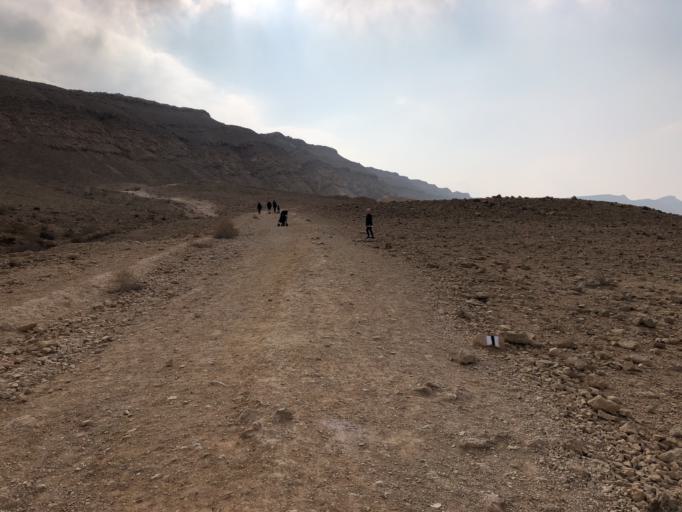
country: IL
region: Southern District
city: Yeroham
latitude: 30.9503
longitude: 35.0253
